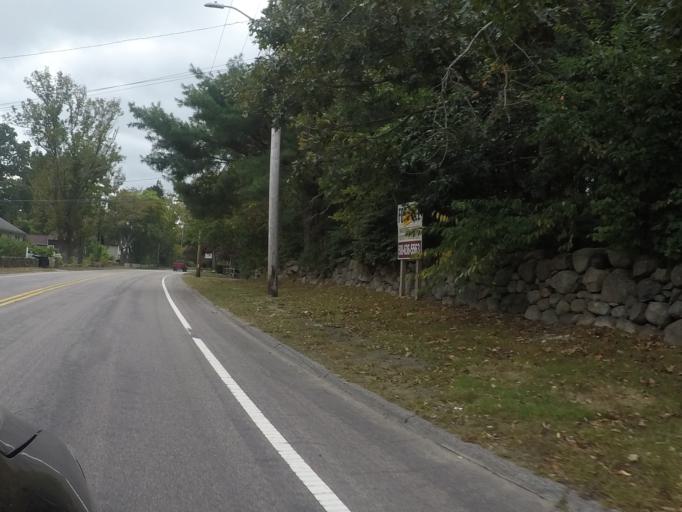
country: US
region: Massachusetts
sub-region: Bristol County
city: Smith Mills
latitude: 41.6372
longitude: -70.9870
